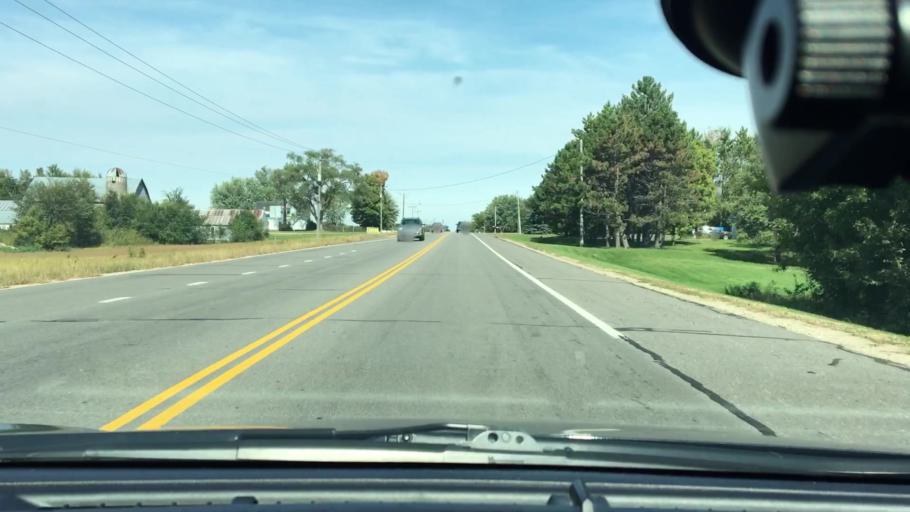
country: US
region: Minnesota
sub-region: Wright County
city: Saint Michael
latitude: 45.1905
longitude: -93.6651
